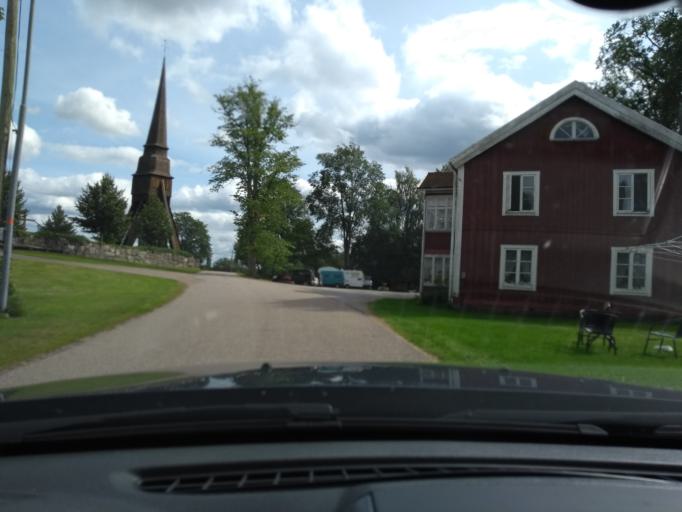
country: SE
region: Joenkoeping
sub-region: Eksjo Kommun
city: Mariannelund
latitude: 57.6273
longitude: 15.7114
